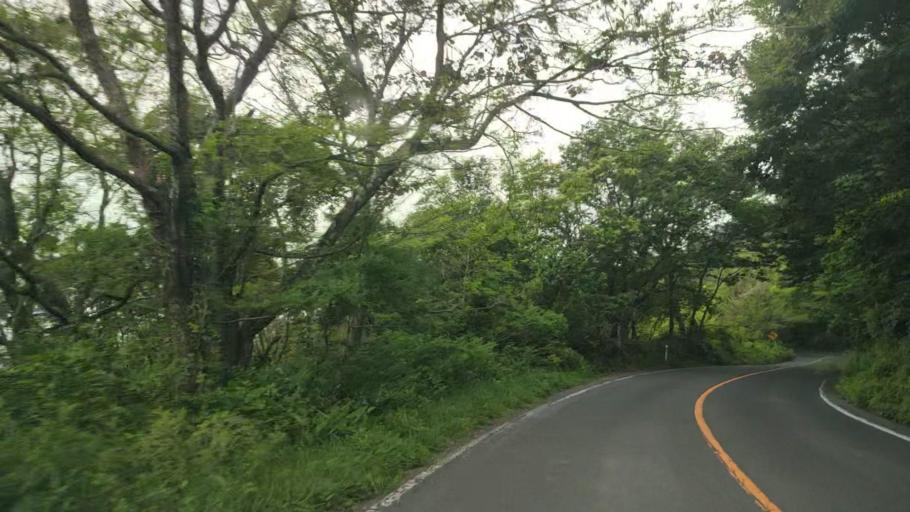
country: JP
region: Tottori
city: Yonago
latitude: 35.3658
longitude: 133.5203
